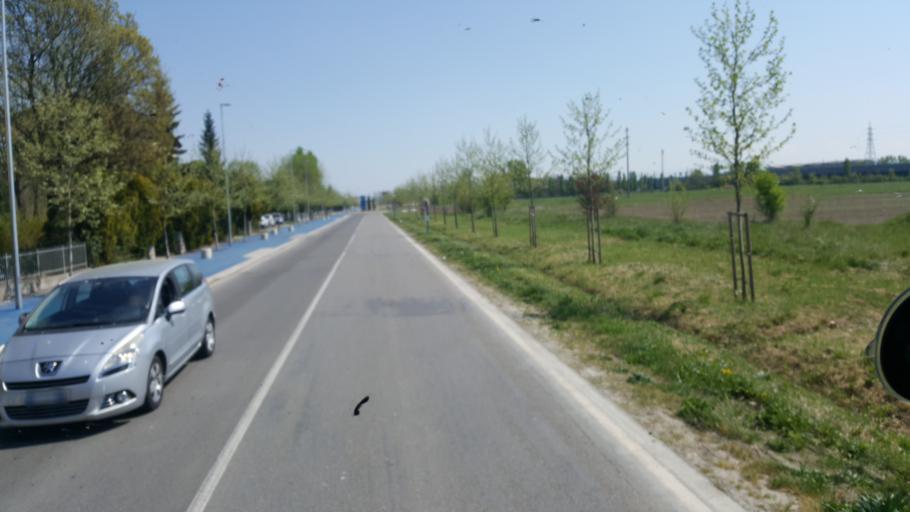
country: IT
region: Emilia-Romagna
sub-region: Provincia di Reggio Emilia
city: Reggio nell'Emilia
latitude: 44.7296
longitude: 10.6459
